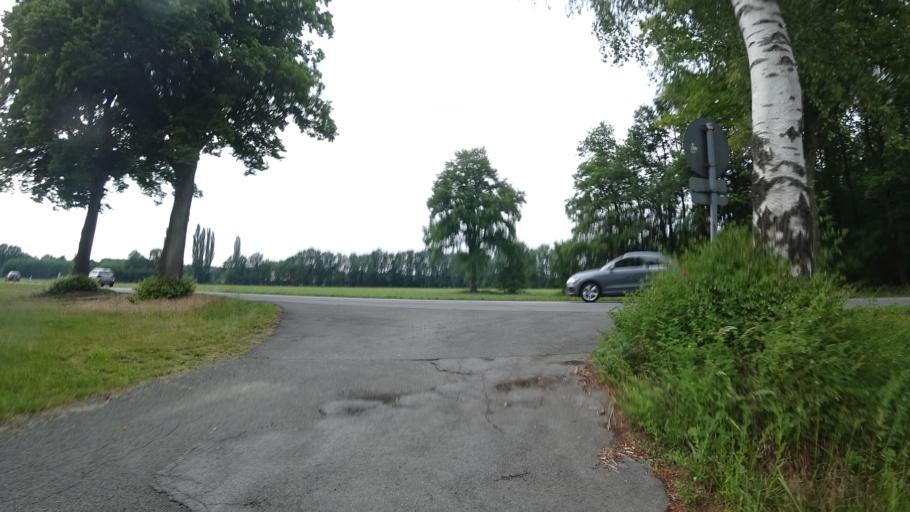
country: DE
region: North Rhine-Westphalia
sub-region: Regierungsbezirk Detmold
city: Guetersloh
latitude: 51.9523
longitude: 8.3415
